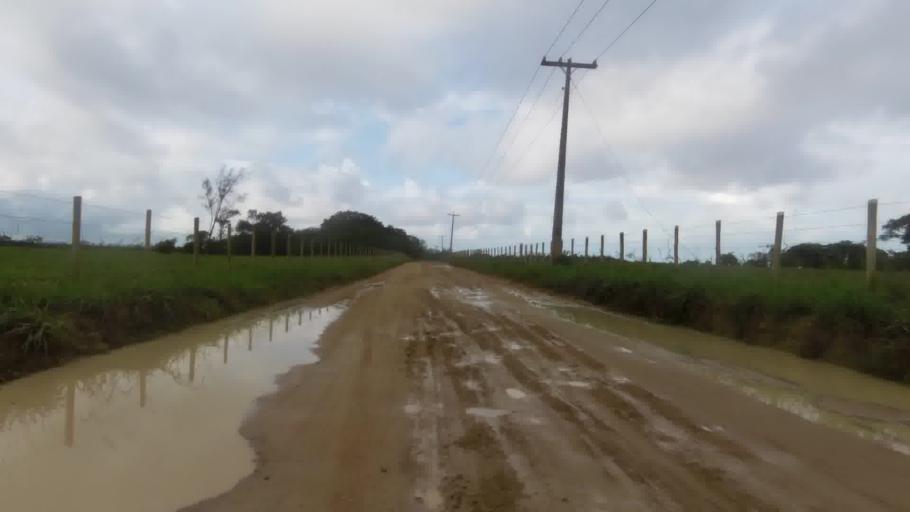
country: BR
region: Espirito Santo
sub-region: Piuma
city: Piuma
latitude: -20.7758
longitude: -40.6302
